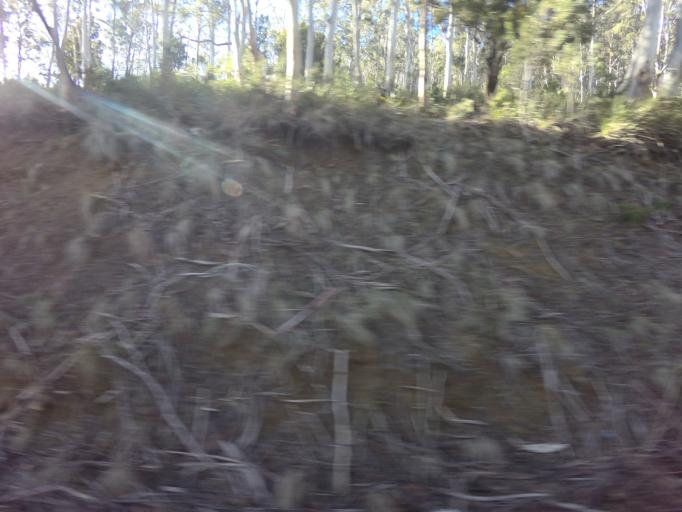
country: AU
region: Tasmania
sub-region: Glenorchy
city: Berriedale
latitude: -42.8193
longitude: 147.1793
